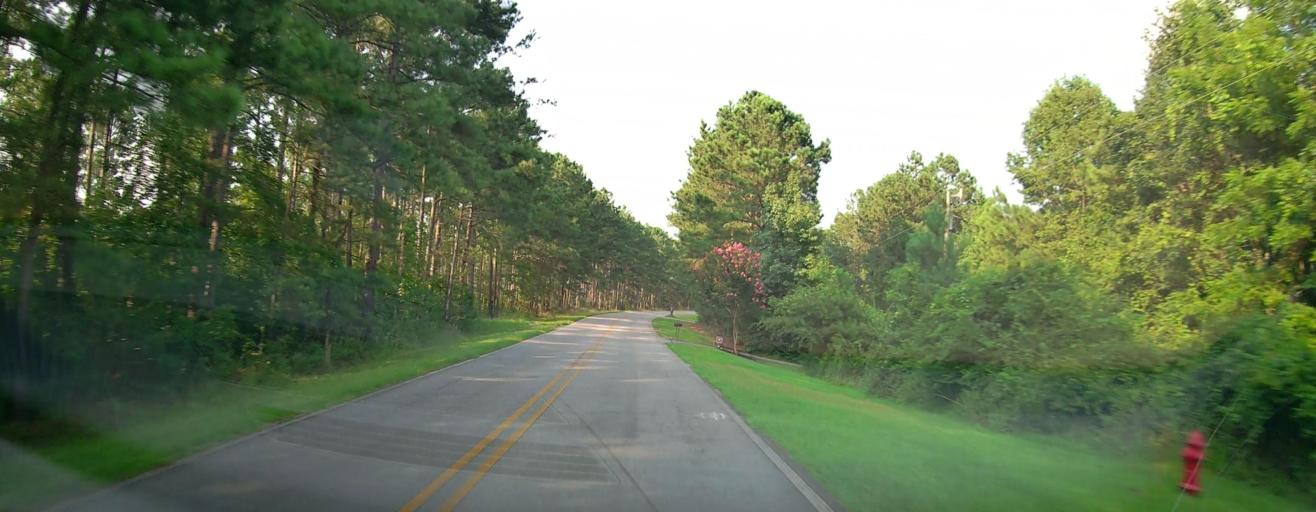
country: US
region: Georgia
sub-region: Monroe County
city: Forsyth
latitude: 32.9983
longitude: -83.7557
